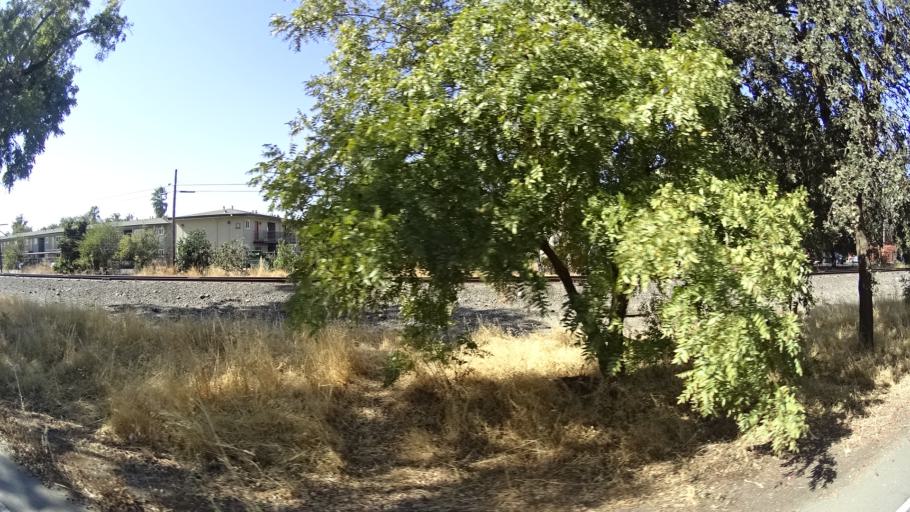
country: US
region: California
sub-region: Yolo County
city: Woodland
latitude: 38.6572
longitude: -121.7658
